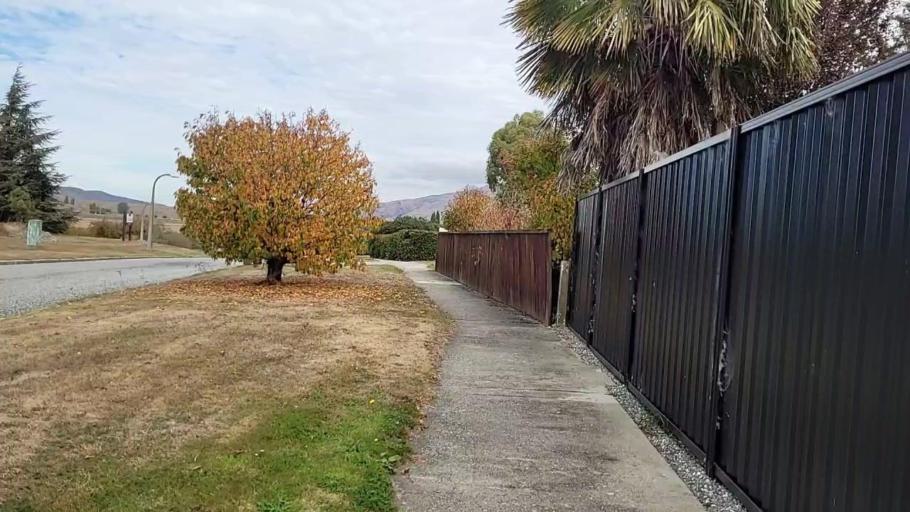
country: NZ
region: Otago
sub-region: Queenstown-Lakes District
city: Kingston
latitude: -45.4794
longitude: 169.3126
